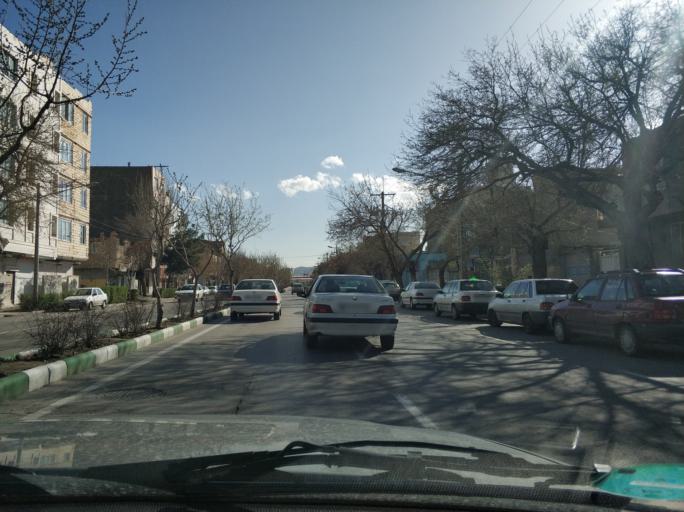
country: IR
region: Razavi Khorasan
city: Mashhad
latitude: 36.3134
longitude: 59.6256
